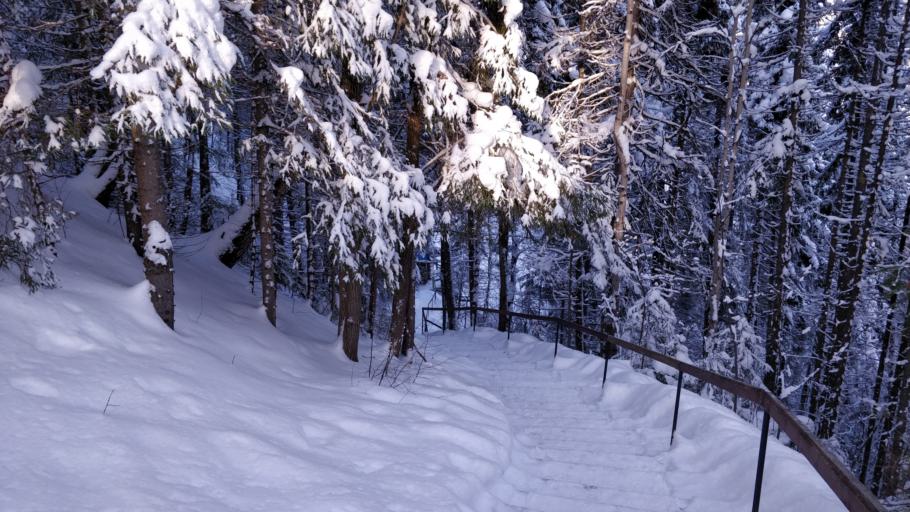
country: RU
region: Perm
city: Verkhnechusovskiye Gorodki
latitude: 58.2120
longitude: 57.0717
